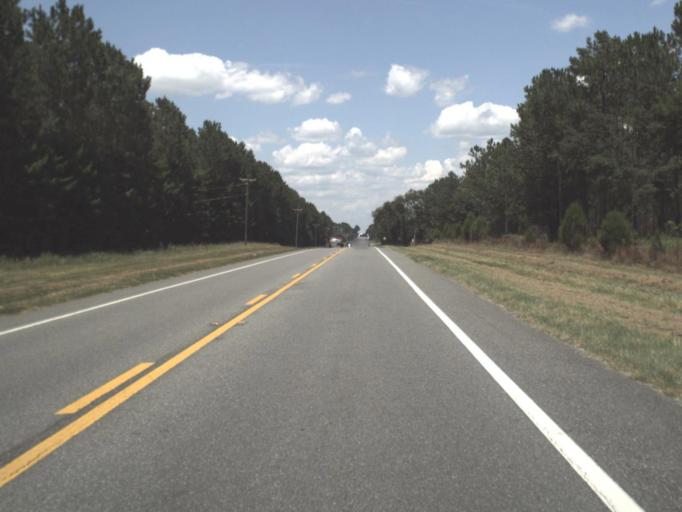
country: US
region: Florida
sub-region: Columbia County
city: Lake City
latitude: 30.1117
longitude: -82.7350
